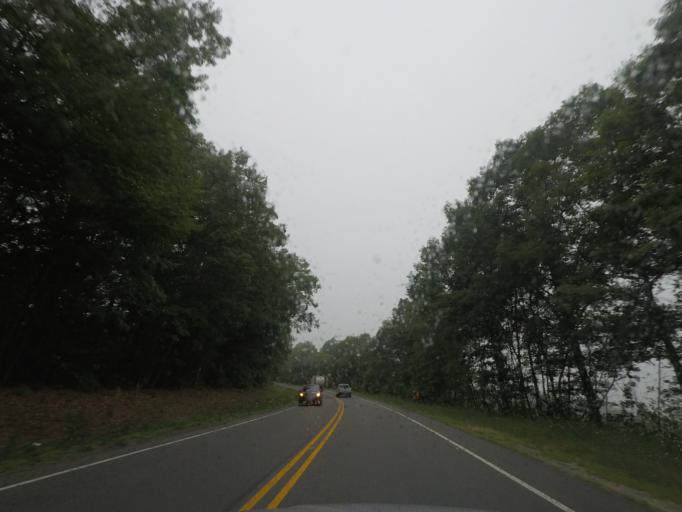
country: US
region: Virginia
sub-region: Buckingham County
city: Buckingham
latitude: 37.5046
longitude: -78.4784
